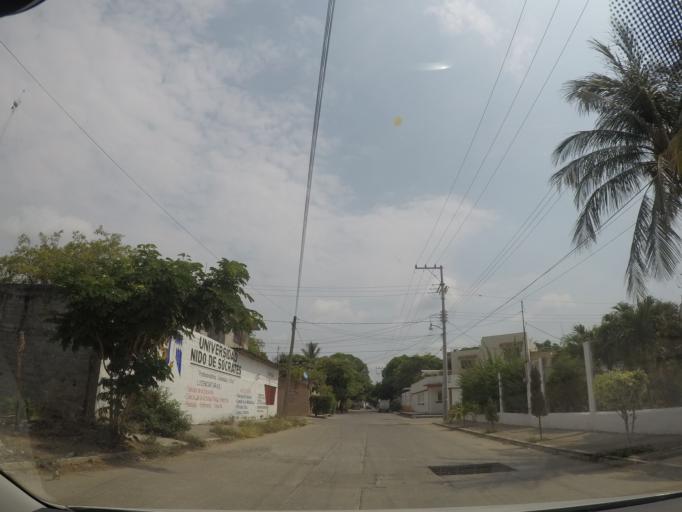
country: MX
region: Oaxaca
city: El Espinal
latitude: 16.4787
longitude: -95.0386
